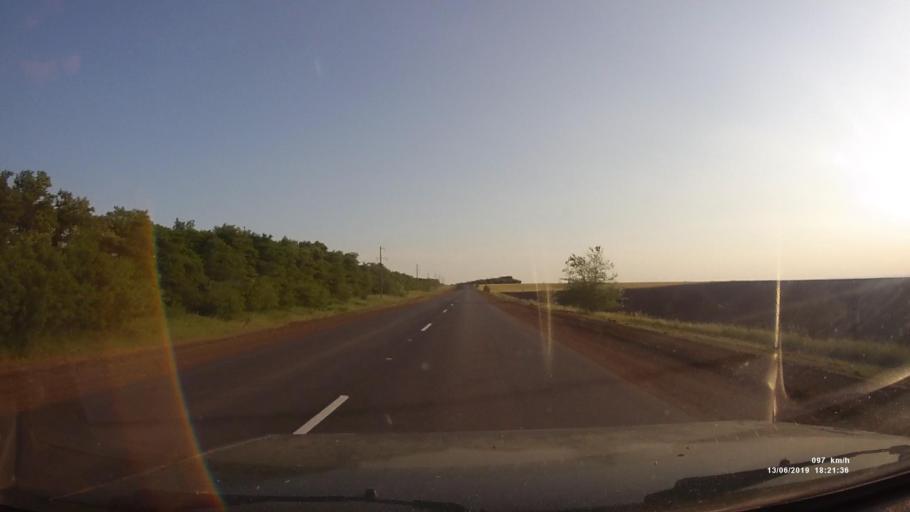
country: RU
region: Rostov
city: Kazanskaya
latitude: 49.8687
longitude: 41.2885
